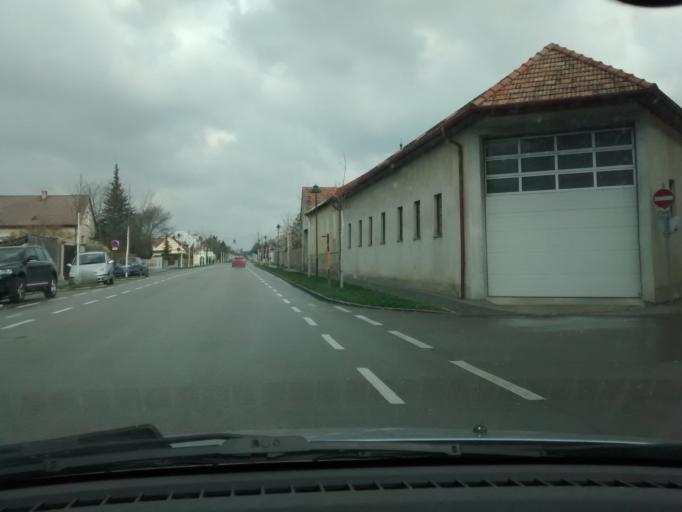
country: AT
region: Lower Austria
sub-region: Politischer Bezirk Modling
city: Laxenburg
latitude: 48.0702
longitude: 16.3551
